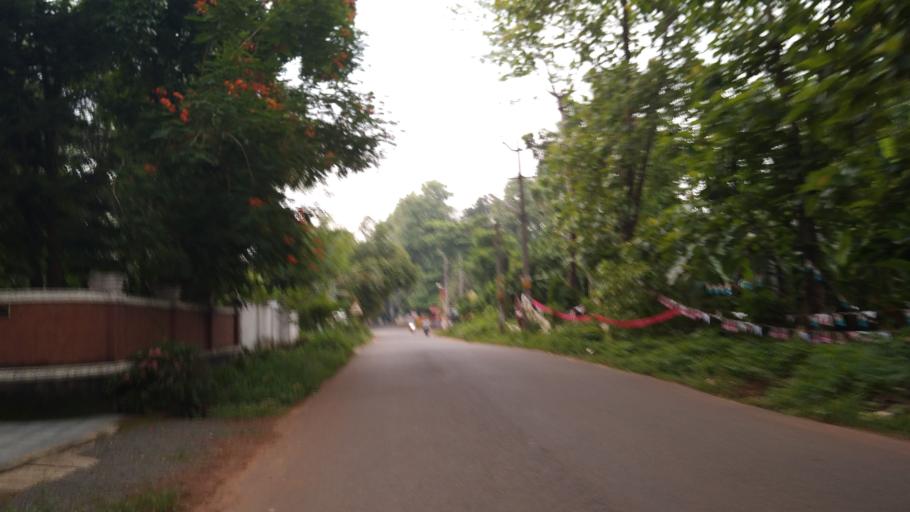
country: IN
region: Kerala
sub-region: Ernakulam
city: Perumbavoor
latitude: 10.0875
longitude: 76.5086
